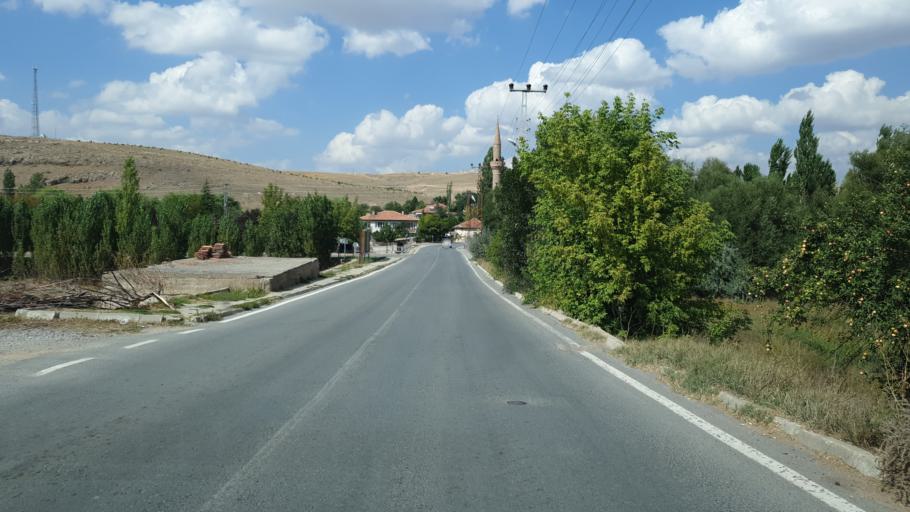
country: TR
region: Kayseri
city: Felahiye
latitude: 39.0919
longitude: 35.5695
